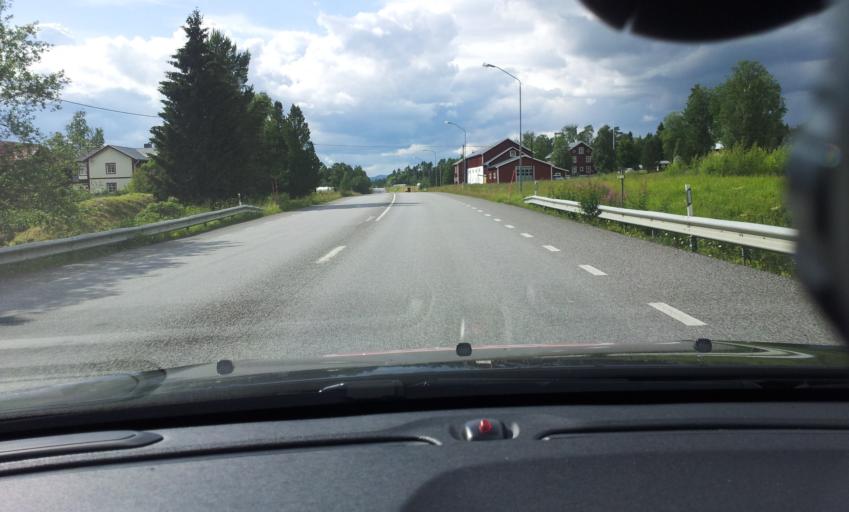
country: SE
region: Jaemtland
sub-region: Are Kommun
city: Jarpen
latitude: 63.3151
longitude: 13.5920
